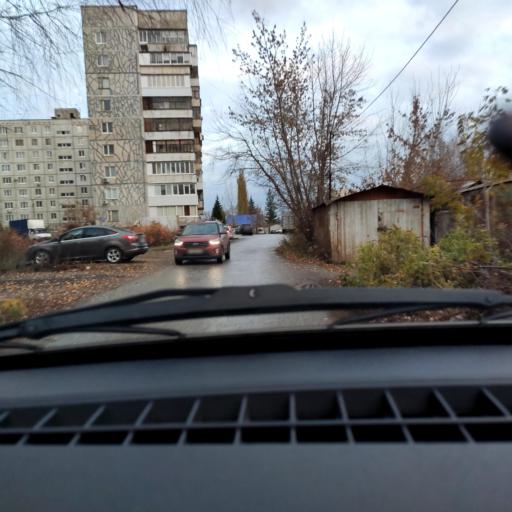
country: RU
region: Bashkortostan
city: Ufa
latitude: 54.7749
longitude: 56.1102
